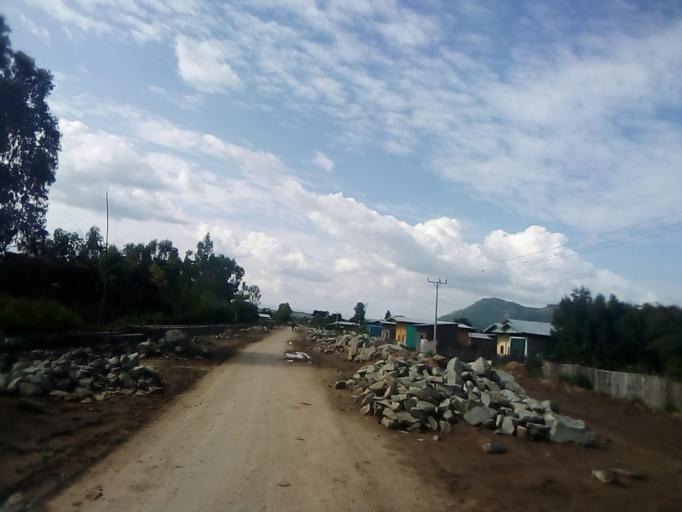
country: ET
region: Southern Nations, Nationalities, and People's Region
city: K'olito
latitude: 7.6041
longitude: 38.0665
